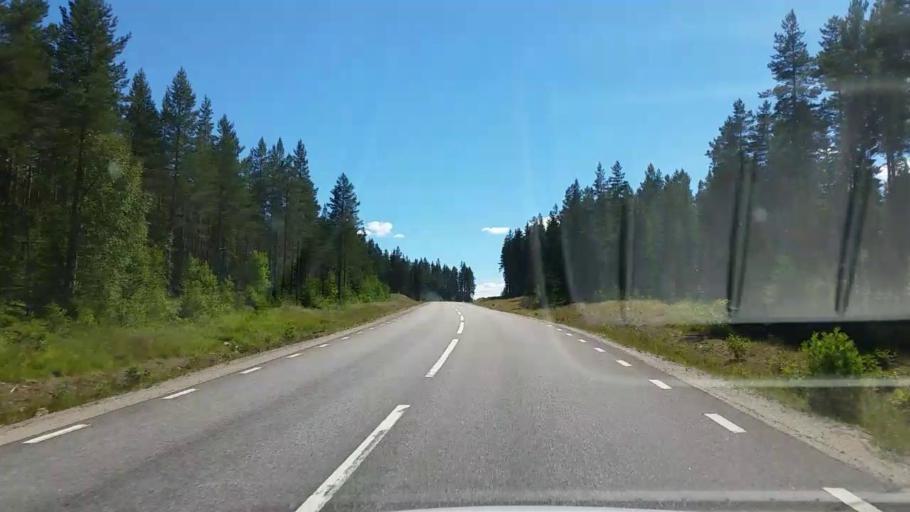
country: SE
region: Gaevleborg
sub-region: Ovanakers Kommun
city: Edsbyn
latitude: 61.0767
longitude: 15.7996
